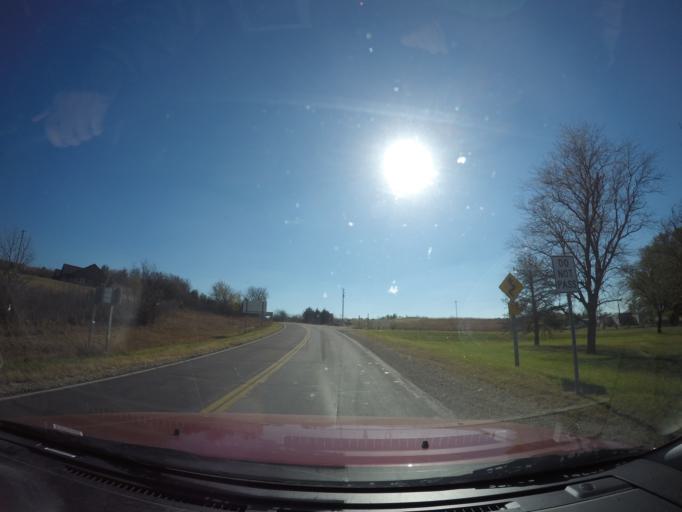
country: US
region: Kansas
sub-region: Geary County
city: Grandview Plaza
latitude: 39.0295
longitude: -96.7834
